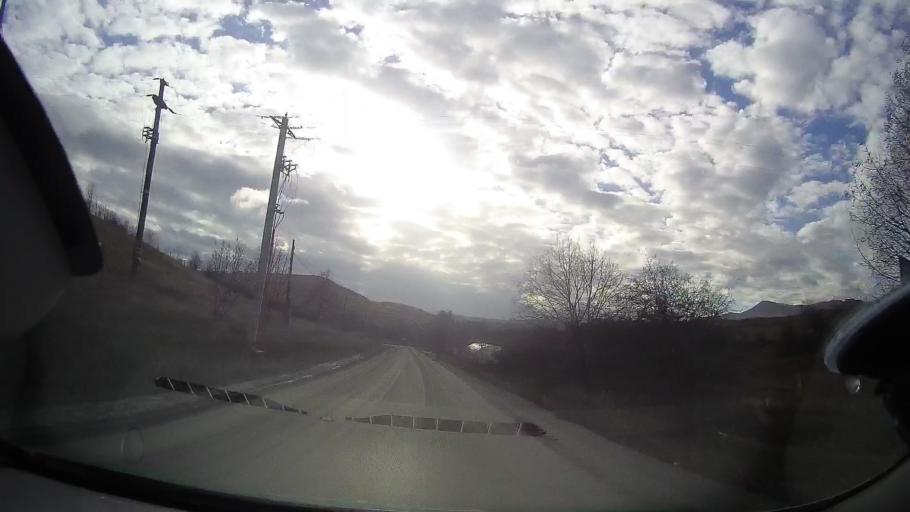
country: RO
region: Cluj
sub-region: Comuna Savadisla
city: Savadisla
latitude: 46.6441
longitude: 23.4646
